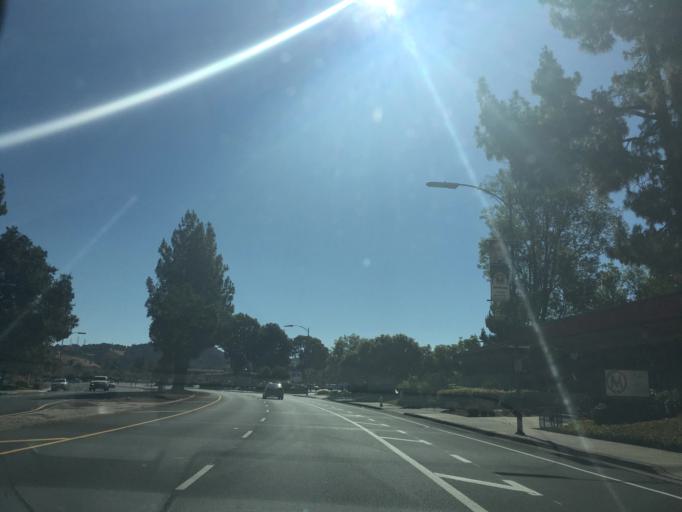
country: US
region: California
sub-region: Santa Clara County
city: Seven Trees
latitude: 37.2207
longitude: -121.8648
